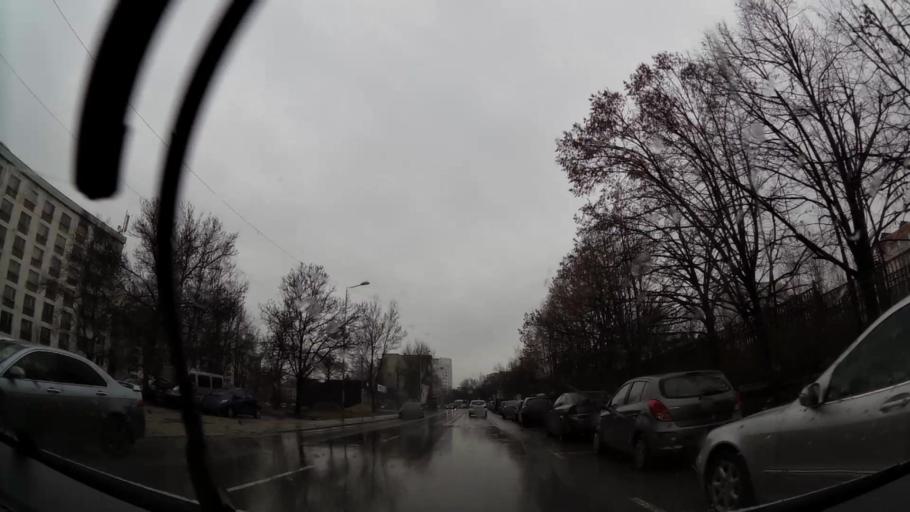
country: BG
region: Sofia-Capital
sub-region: Stolichna Obshtina
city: Sofia
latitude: 42.6494
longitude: 23.3417
